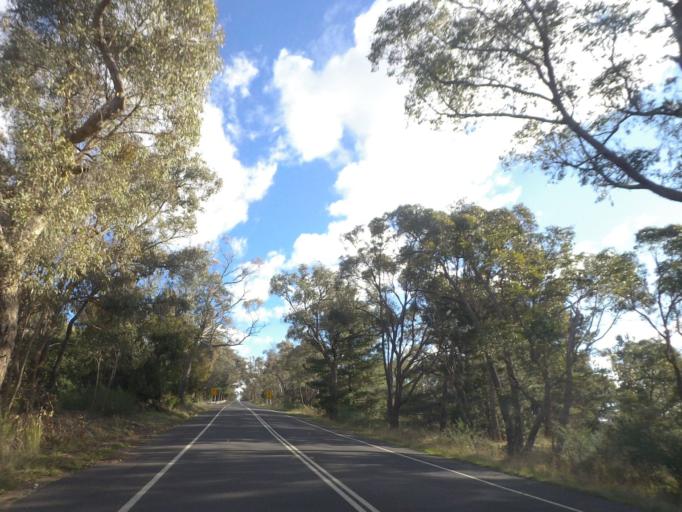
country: AU
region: Victoria
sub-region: Mount Alexander
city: Castlemaine
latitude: -37.1040
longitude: 144.3137
